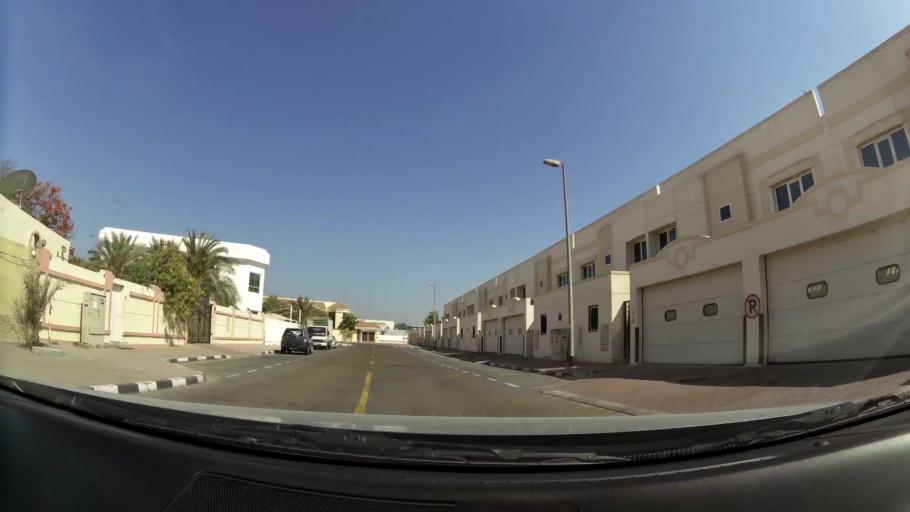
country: AE
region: Ash Shariqah
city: Sharjah
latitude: 25.2468
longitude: 55.2836
